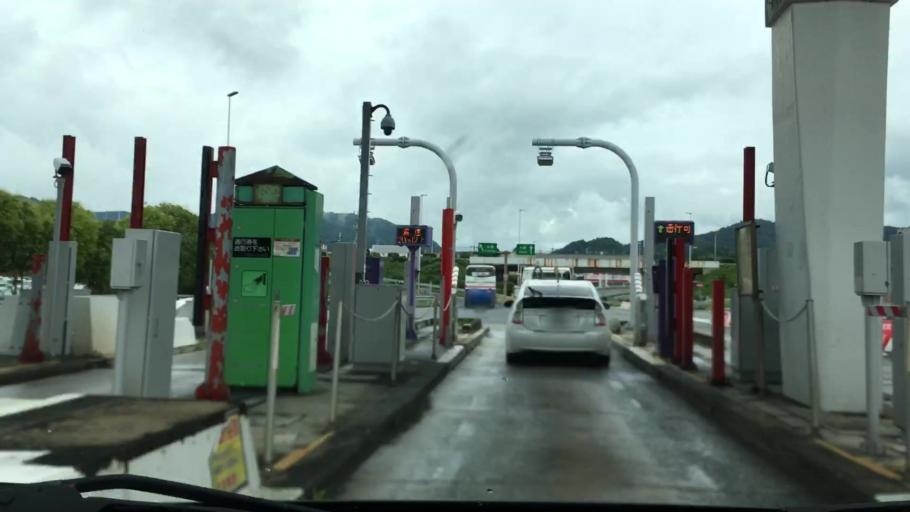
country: JP
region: Hyogo
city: Himeji
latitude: 34.9471
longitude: 134.7616
